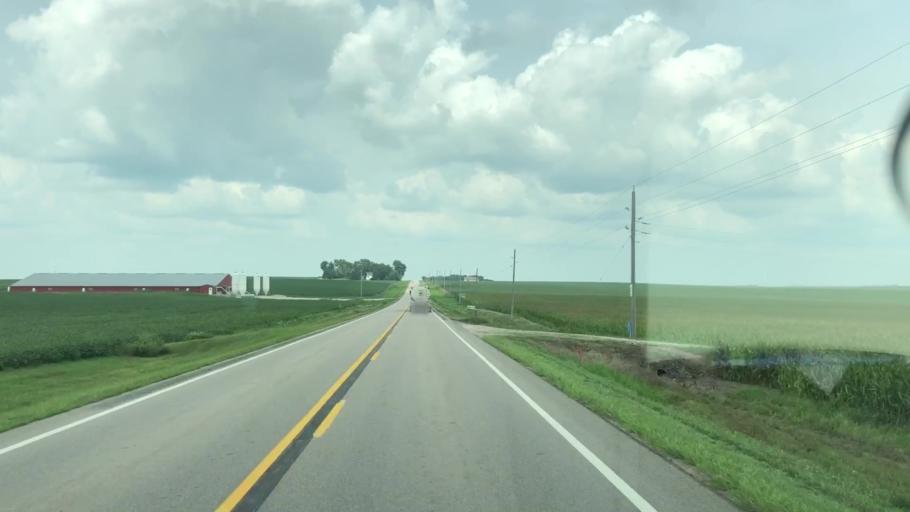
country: US
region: Iowa
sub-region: Plymouth County
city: Remsen
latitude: 42.7833
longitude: -95.9579
